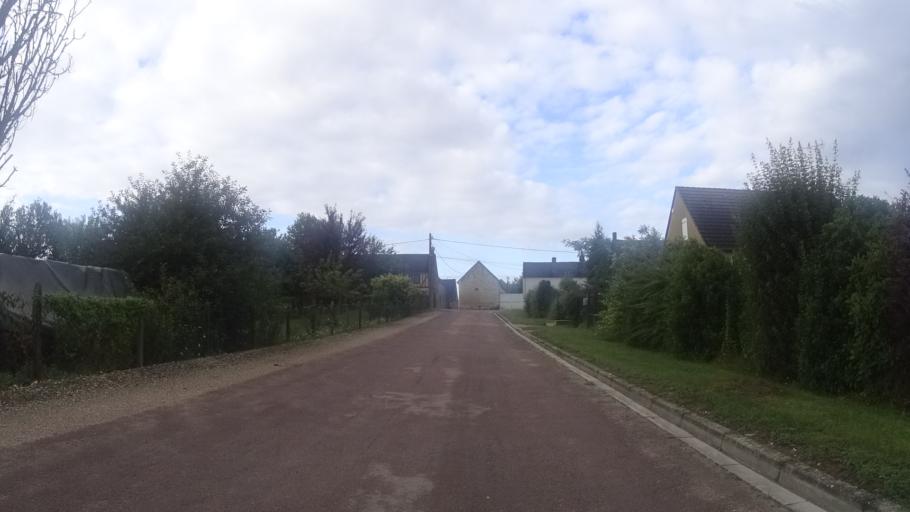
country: FR
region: Bourgogne
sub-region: Departement de l'Yonne
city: Joigny
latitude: 47.9528
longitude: 3.4132
